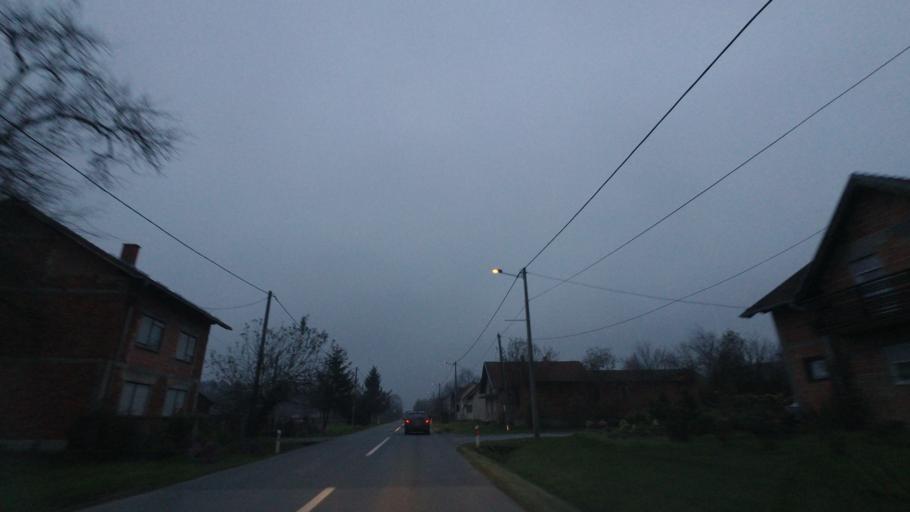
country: HR
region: Sisacko-Moslavacka
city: Glina
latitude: 45.3728
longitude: 16.1337
